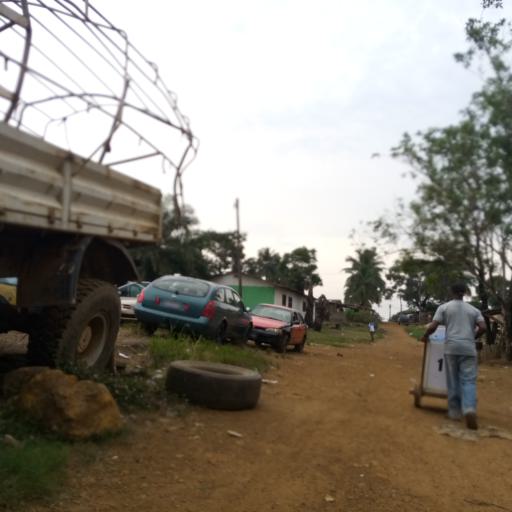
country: LR
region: Montserrado
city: Monrovia
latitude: 6.3004
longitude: -10.6898
